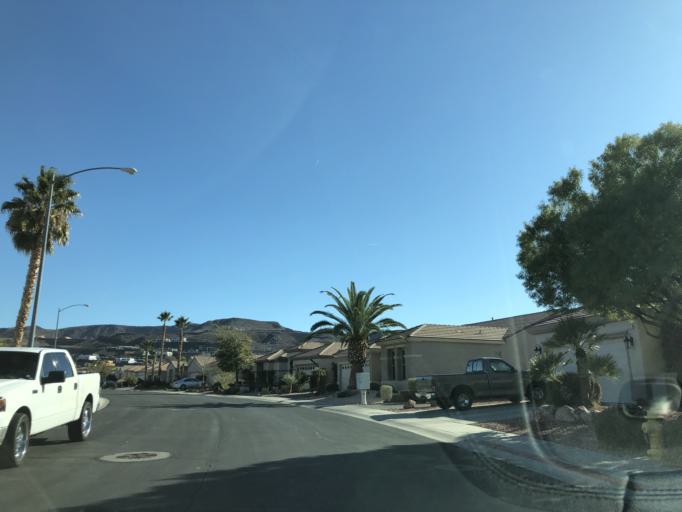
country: US
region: Nevada
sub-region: Clark County
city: Whitney
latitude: 36.0044
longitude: -115.0721
